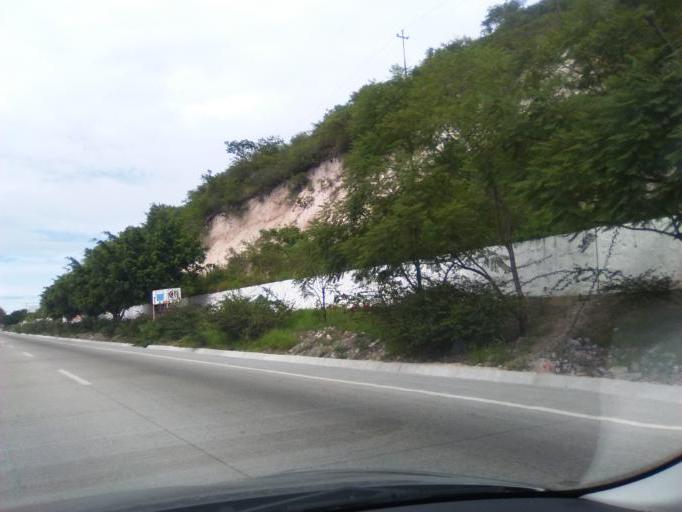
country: MX
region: Guerrero
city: Chilpancingo de los Bravos
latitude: 17.5941
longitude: -99.5183
